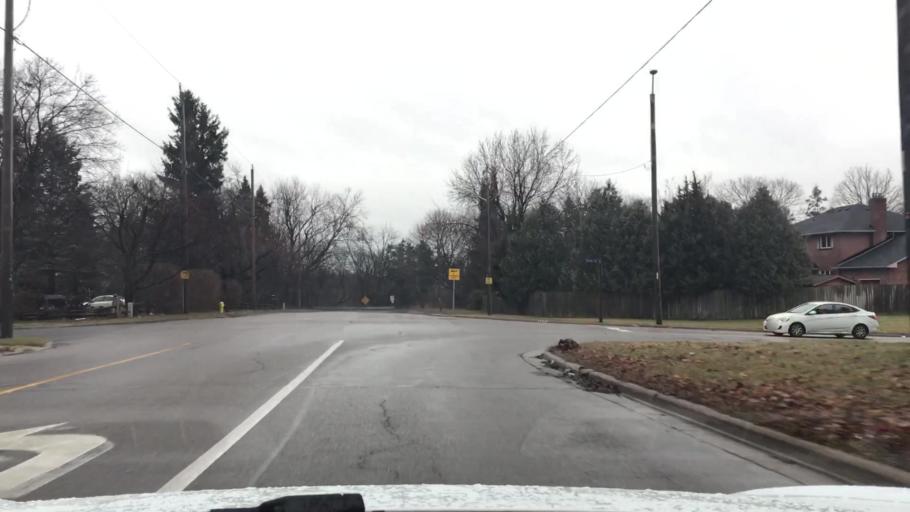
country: CA
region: Ontario
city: Oshawa
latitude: 43.8997
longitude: -78.8104
